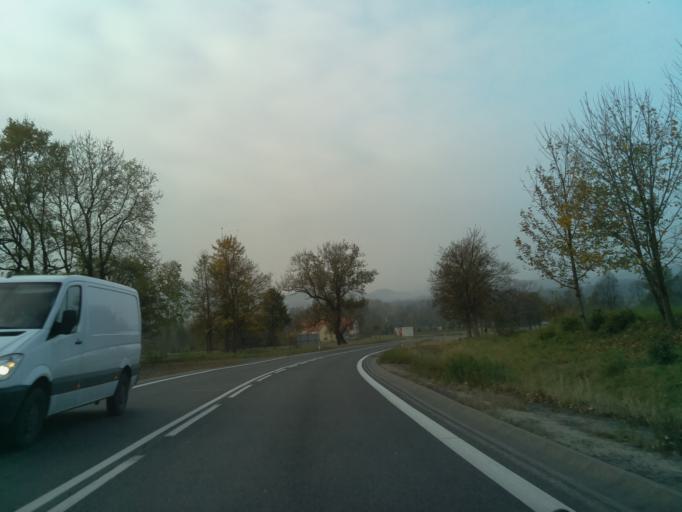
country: PL
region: Lower Silesian Voivodeship
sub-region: Powiat jeleniogorski
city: Janowice Wielkie
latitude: 50.9040
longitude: 15.9075
